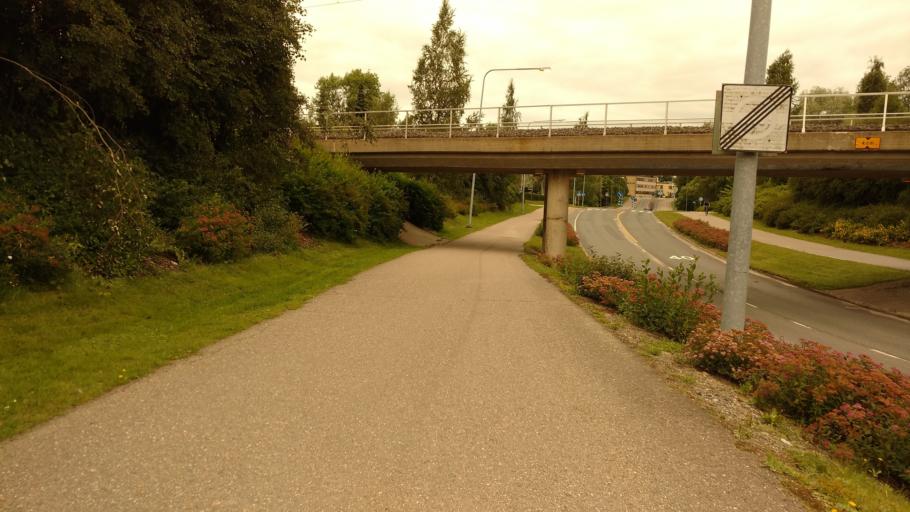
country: FI
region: Varsinais-Suomi
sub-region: Turku
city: Paimio
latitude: 60.4593
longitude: 22.6828
